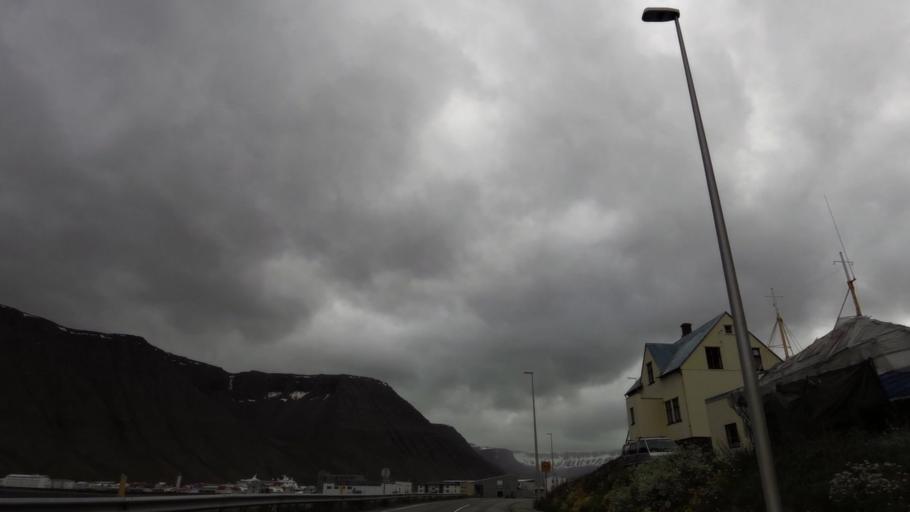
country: IS
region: Westfjords
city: Isafjoerdur
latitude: 66.0807
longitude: -23.1239
